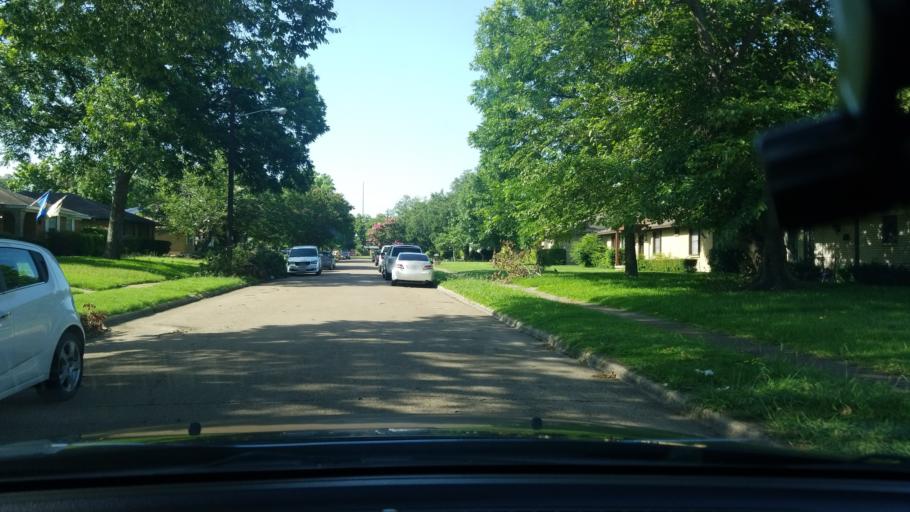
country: US
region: Texas
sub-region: Dallas County
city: Mesquite
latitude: 32.8094
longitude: -96.6792
